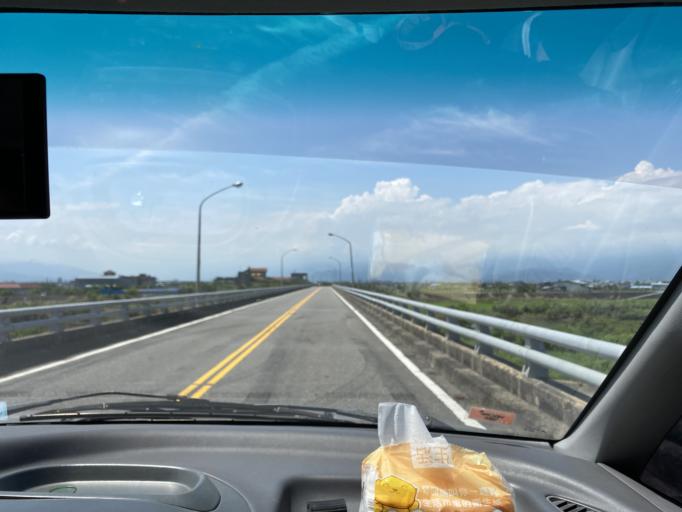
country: TW
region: Taiwan
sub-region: Yilan
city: Yilan
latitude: 24.7237
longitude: 121.8183
